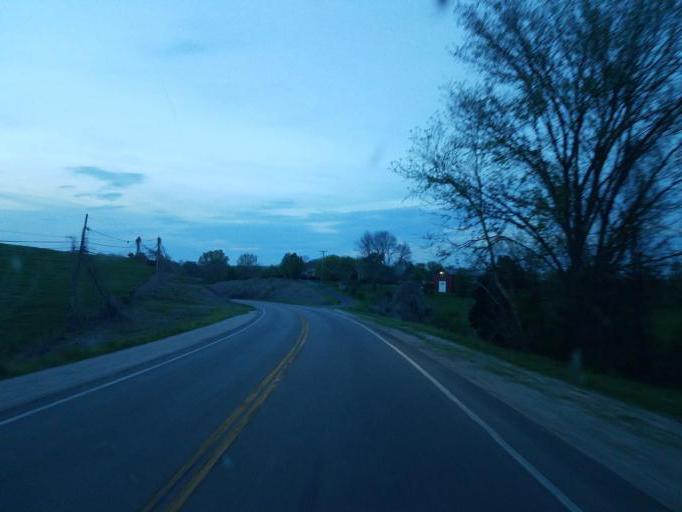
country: US
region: Kentucky
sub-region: Hart County
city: Munfordville
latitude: 37.2645
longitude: -85.8810
